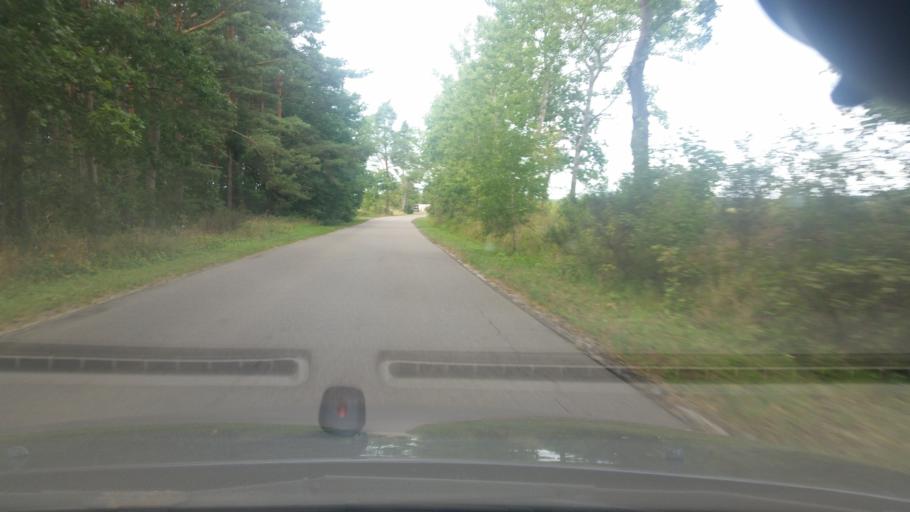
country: PL
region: Pomeranian Voivodeship
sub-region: Powiat leborski
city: Leba
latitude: 54.7274
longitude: 17.6123
